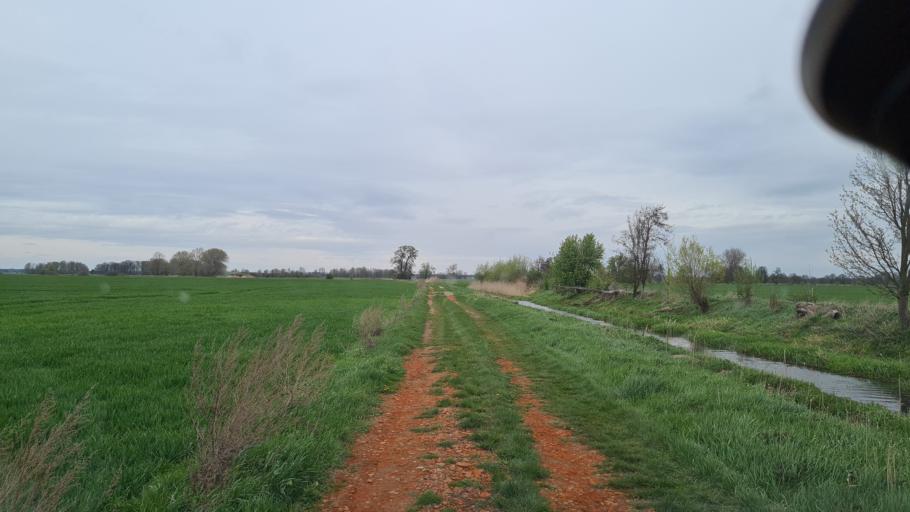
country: DE
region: Brandenburg
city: Doberlug-Kirchhain
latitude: 51.6613
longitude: 13.5658
